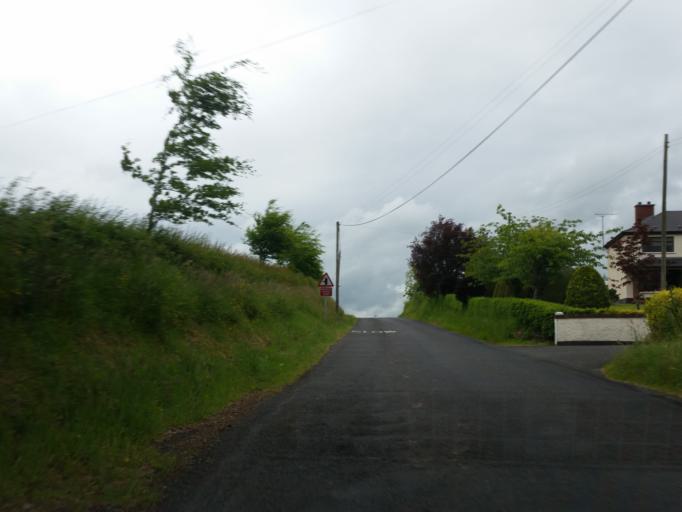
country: IE
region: Ulster
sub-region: County Monaghan
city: Clones
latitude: 54.2254
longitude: -7.2569
